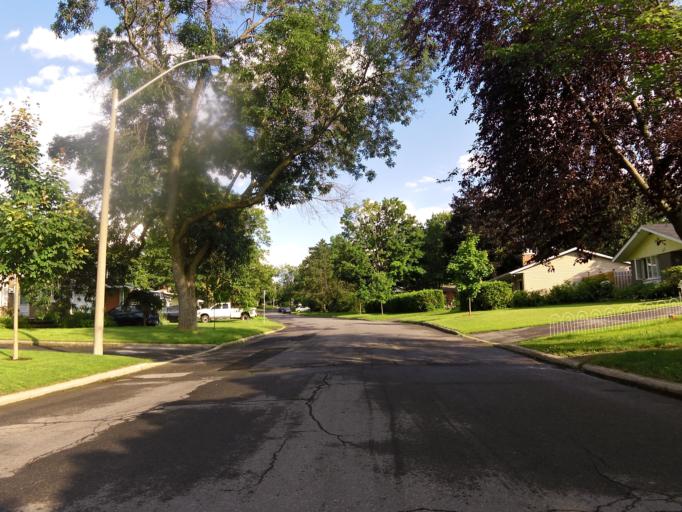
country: CA
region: Ontario
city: Bells Corners
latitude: 45.3460
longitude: -75.7821
